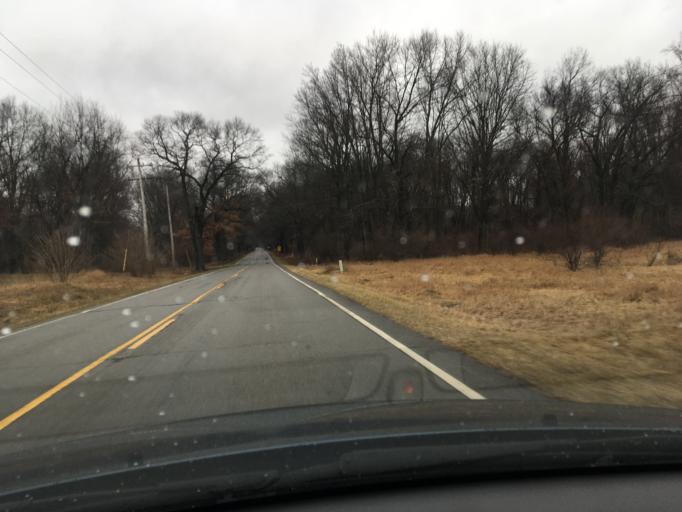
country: US
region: Michigan
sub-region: Jackson County
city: Grass Lake
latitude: 42.3213
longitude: -84.1557
